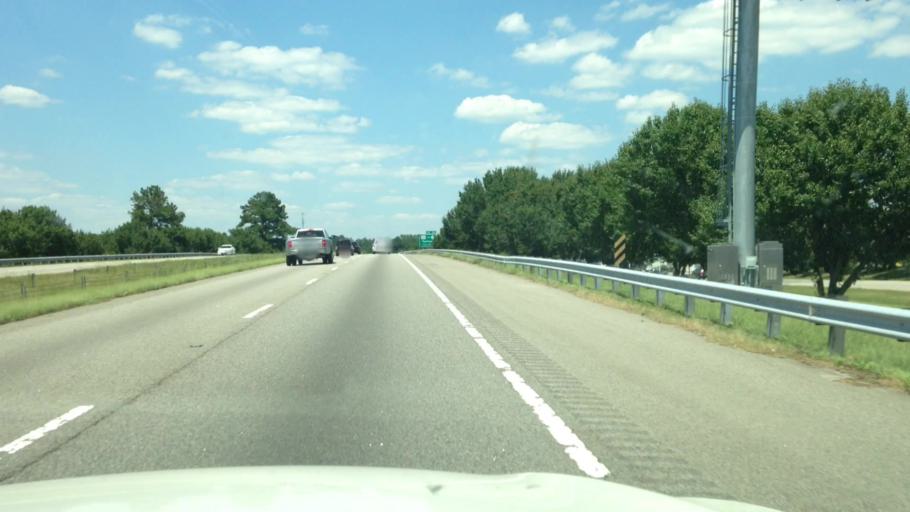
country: US
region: North Carolina
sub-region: Robeson County
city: Saint Pauls
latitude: 34.8091
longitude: -78.9870
